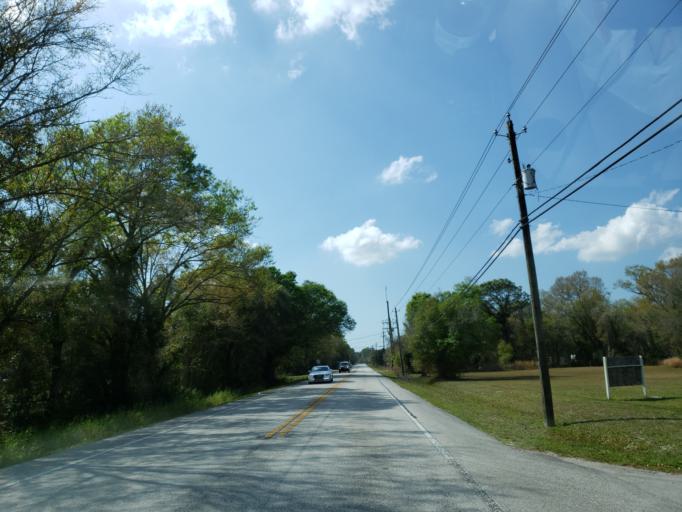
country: US
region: Florida
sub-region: Hillsborough County
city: Keystone
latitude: 28.1432
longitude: -82.6111
